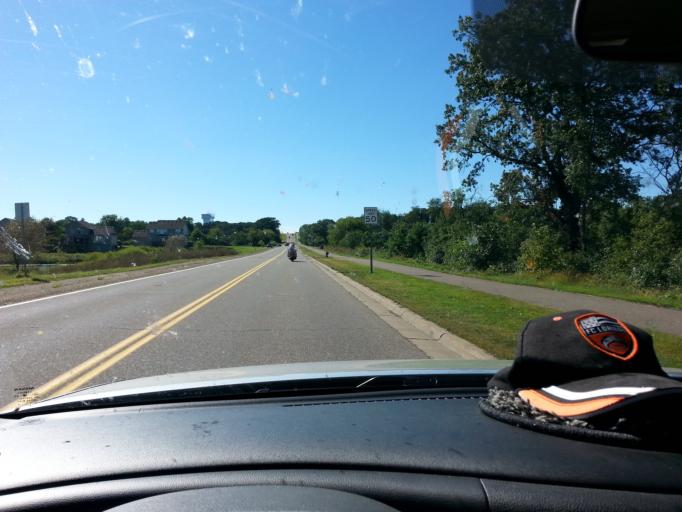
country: US
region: Minnesota
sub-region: Dakota County
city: Farmington
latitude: 44.6670
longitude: -93.1602
